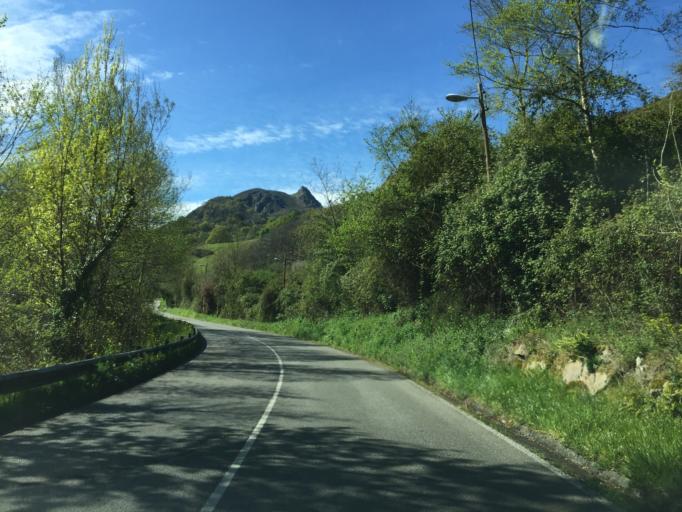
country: ES
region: Asturias
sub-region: Province of Asturias
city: Proaza
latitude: 43.3240
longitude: -5.9927
